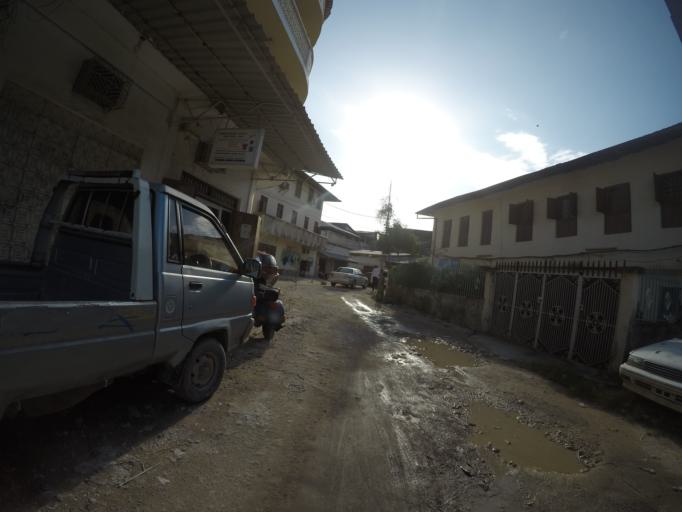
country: TZ
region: Zanzibar Urban/West
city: Zanzibar
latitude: -6.1641
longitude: 39.1924
